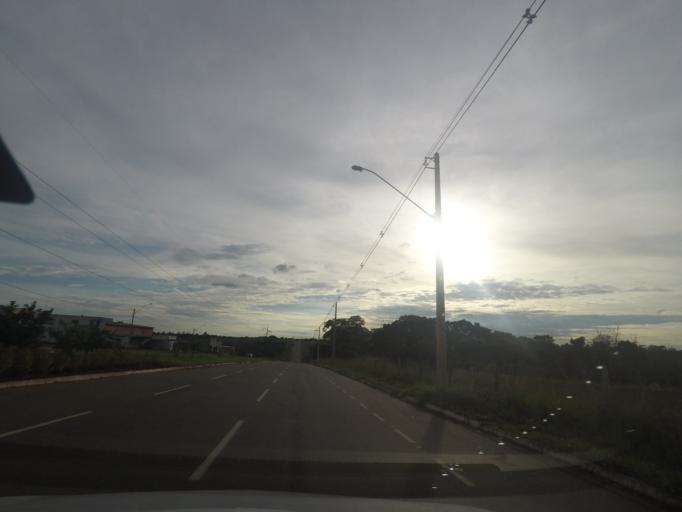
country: BR
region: Goias
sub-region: Trindade
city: Trindade
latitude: -16.7190
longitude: -49.3925
